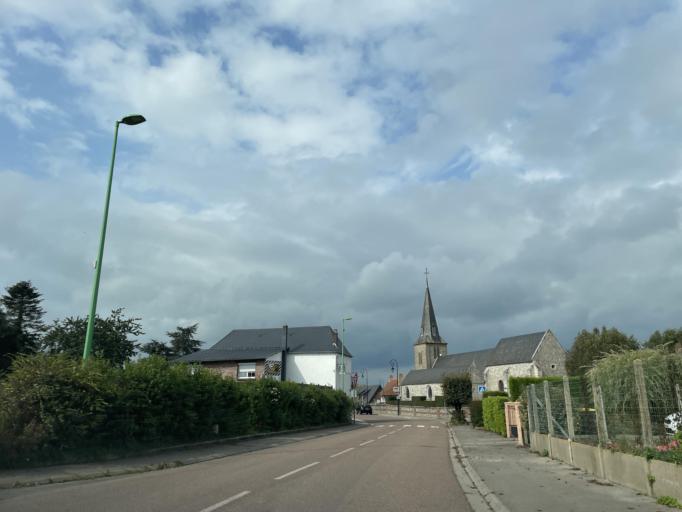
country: FR
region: Haute-Normandie
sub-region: Departement de la Seine-Maritime
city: Saint-Martin-en-Campagne
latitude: 49.9562
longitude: 1.2243
